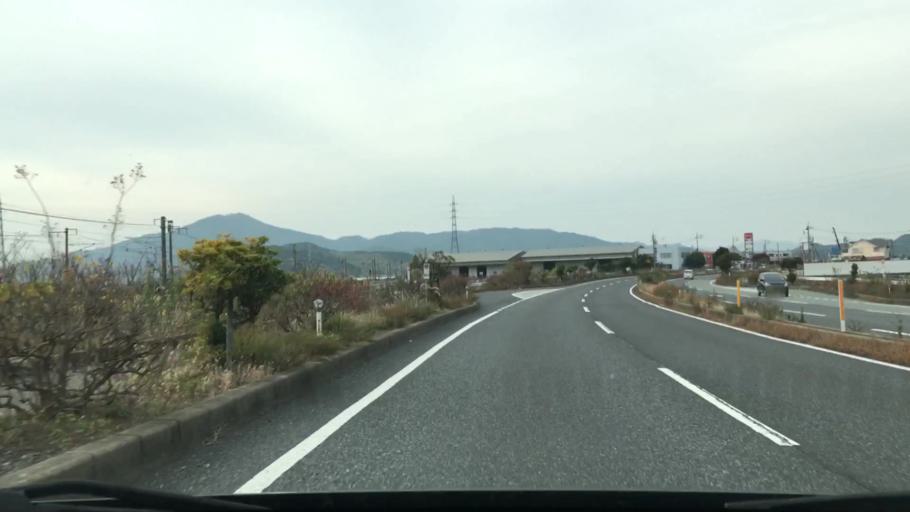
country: JP
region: Yamaguchi
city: Hofu
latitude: 34.0478
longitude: 131.5057
